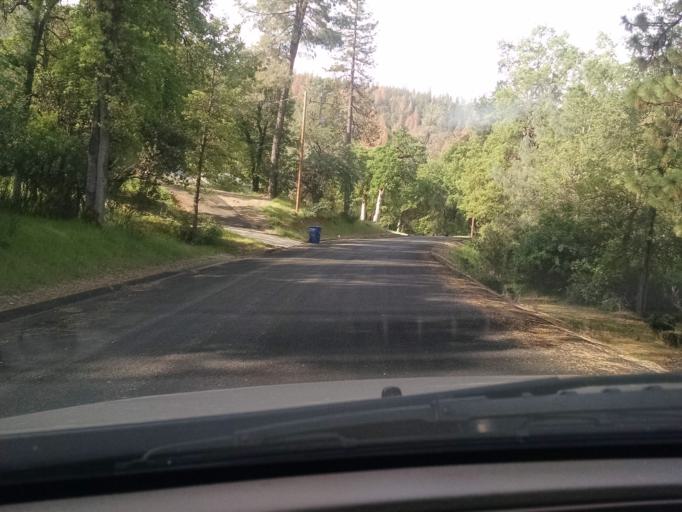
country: US
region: California
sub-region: Madera County
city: Oakhurst
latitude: 37.2834
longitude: -119.6262
